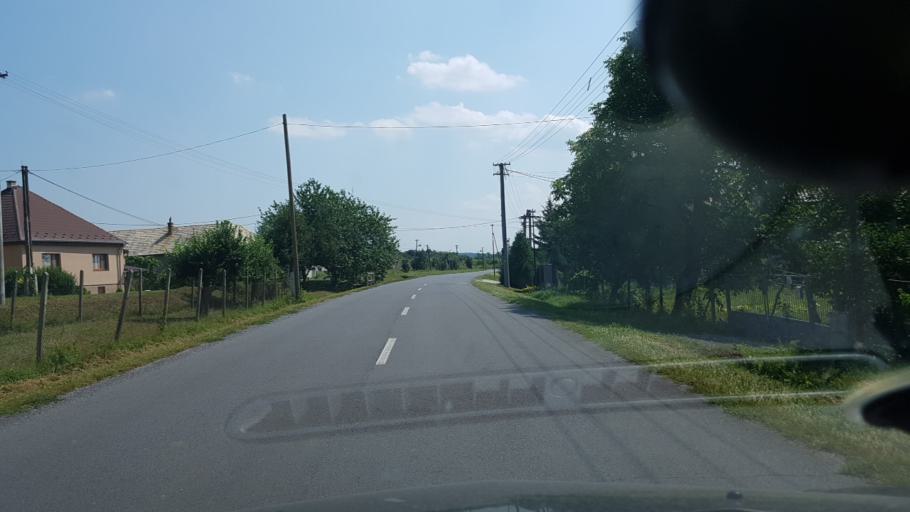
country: SK
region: Banskobystricky
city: Velky Krtis
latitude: 48.2792
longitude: 19.4308
